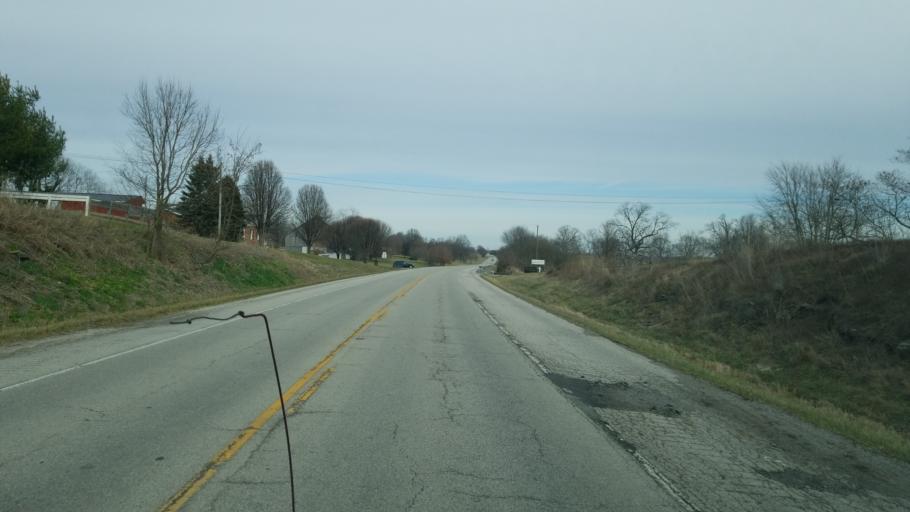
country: US
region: Kentucky
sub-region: Fleming County
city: Flemingsburg
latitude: 38.5075
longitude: -83.8482
